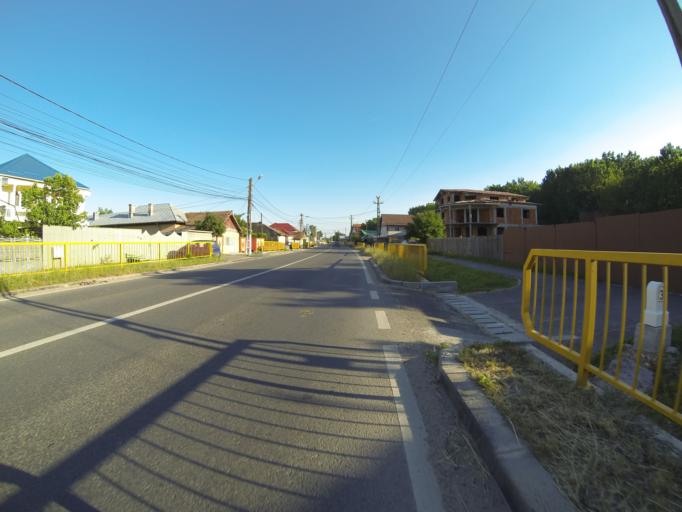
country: RO
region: Dolj
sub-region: Comuna Podari
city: Podari
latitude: 44.2684
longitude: 23.7878
